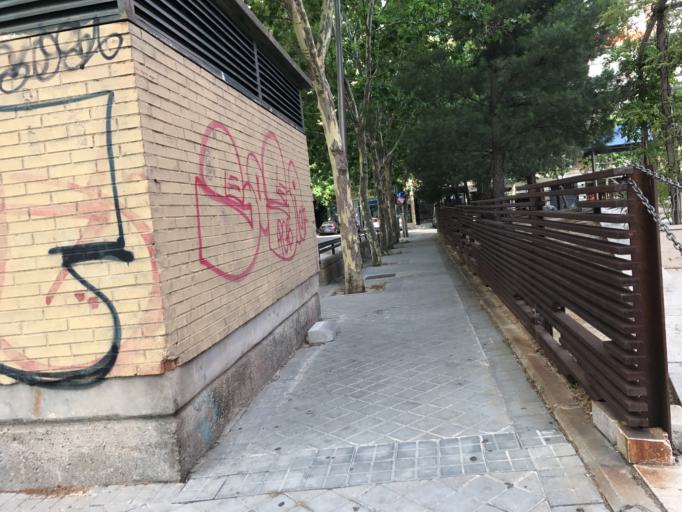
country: ES
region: Madrid
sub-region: Provincia de Madrid
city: Salamanca
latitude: 40.4406
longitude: -3.6705
